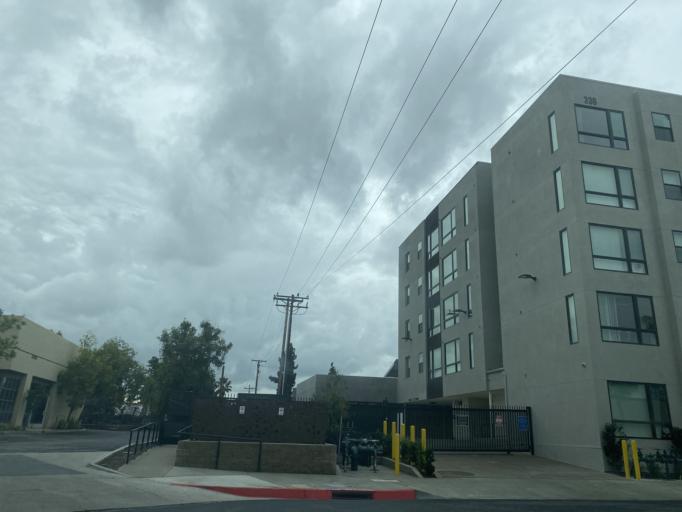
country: US
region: California
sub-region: Orange County
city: Fullerton
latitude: 33.8694
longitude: -117.9177
